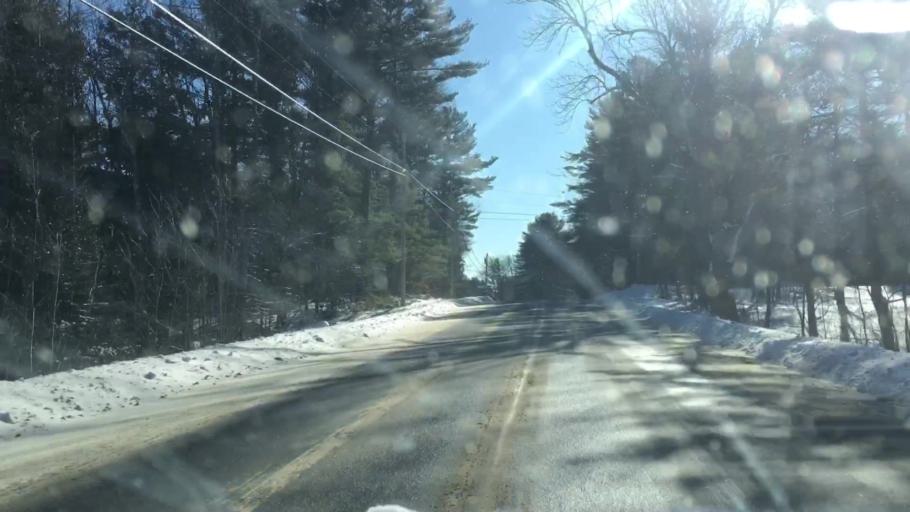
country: US
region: Maine
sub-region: Sagadahoc County
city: Topsham
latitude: 43.9257
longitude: -70.0463
